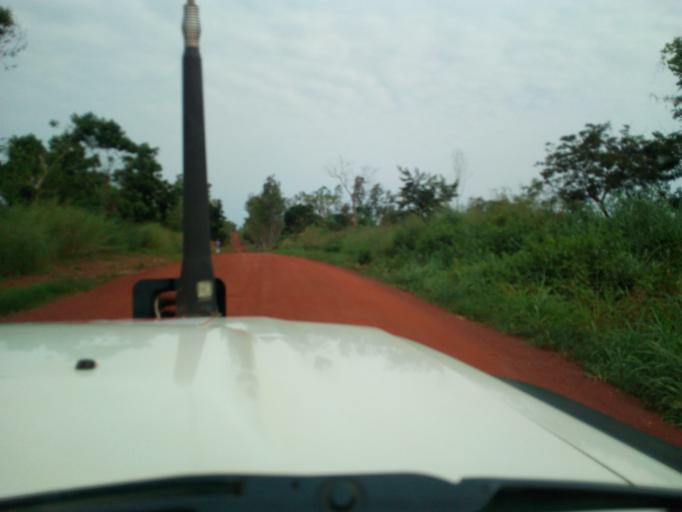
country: CF
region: Ouaka
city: Bambari
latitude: 5.7882
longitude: 20.6433
